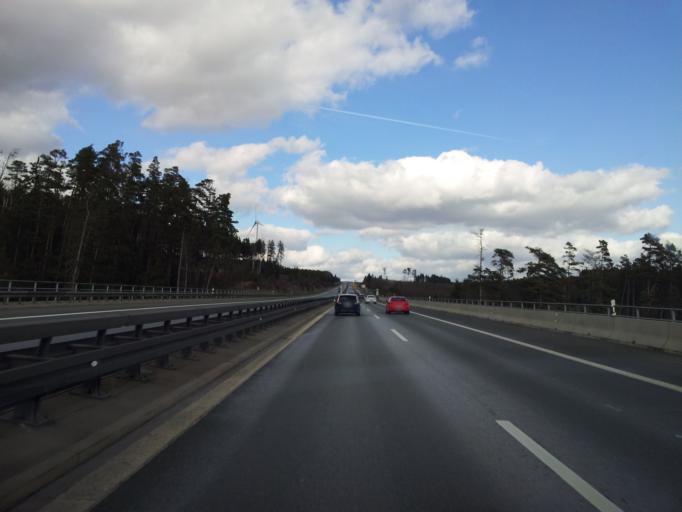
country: DE
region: Bavaria
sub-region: Upper Franconia
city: Topen
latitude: 50.3554
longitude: 11.8684
